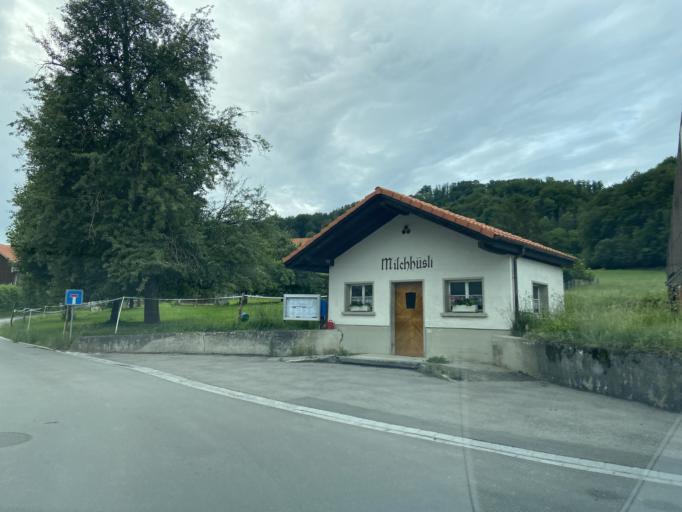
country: CH
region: Thurgau
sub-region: Muenchwilen District
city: Aadorf
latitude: 47.4563
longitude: 8.9095
